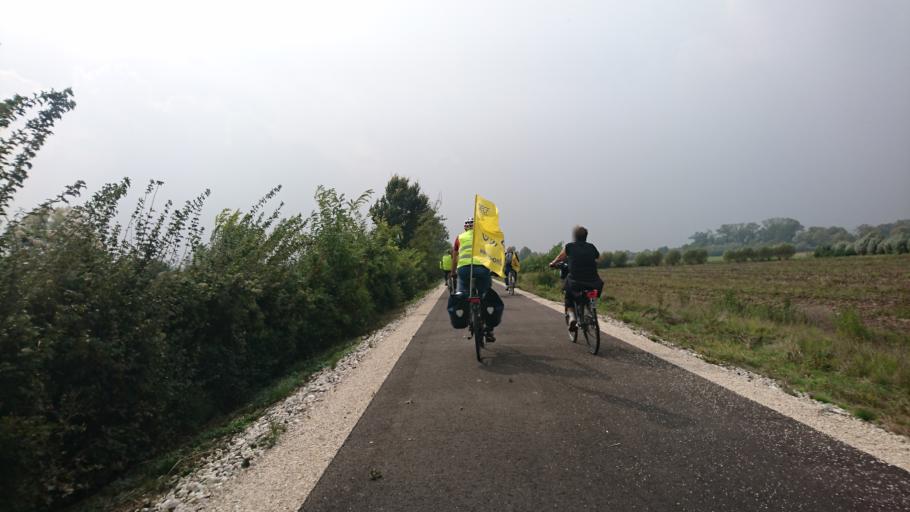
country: IT
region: Veneto
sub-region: Provincia di Vicenza
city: Grisignano di Zocco
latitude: 45.4900
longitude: 11.6919
